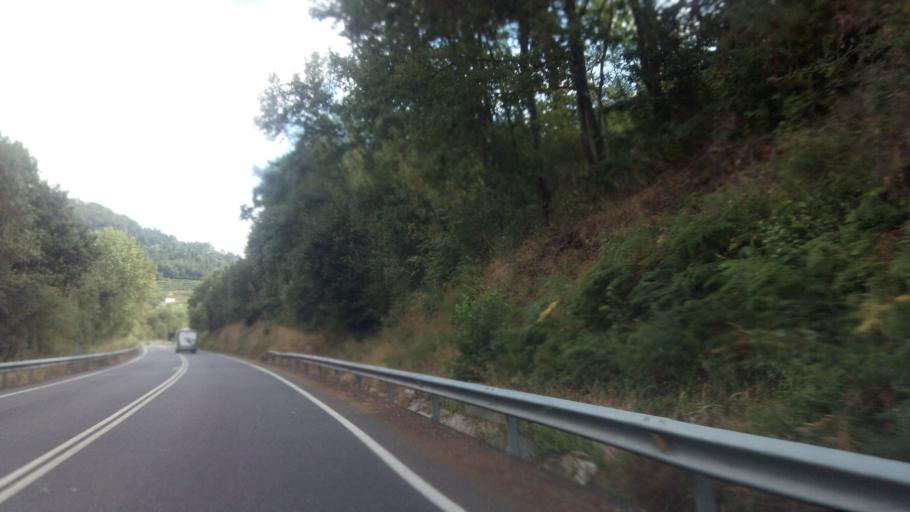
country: ES
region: Galicia
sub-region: Provincia de Ourense
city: Nogueira de Ramuin
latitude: 42.4151
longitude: -7.7791
